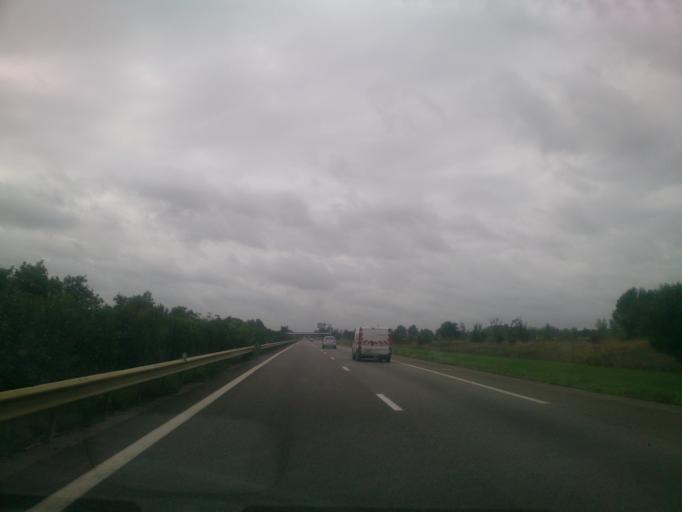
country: FR
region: Midi-Pyrenees
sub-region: Departement de la Haute-Garonne
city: Le Fauga
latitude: 43.3889
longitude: 1.2845
